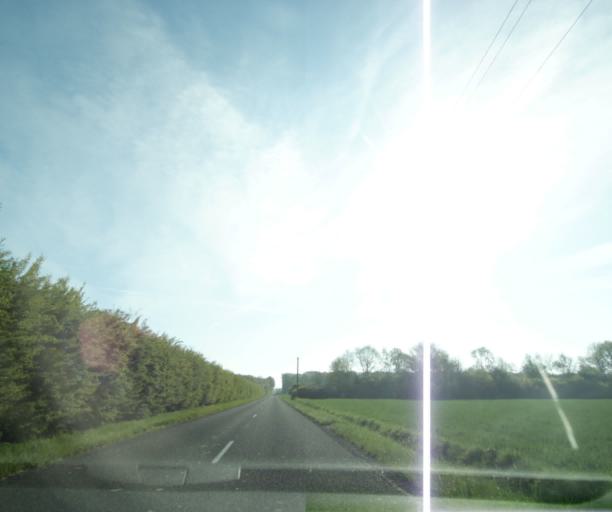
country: FR
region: Ile-de-France
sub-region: Departement de Seine-et-Marne
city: La Chapelle-Gauthier
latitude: 48.5136
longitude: 2.9434
